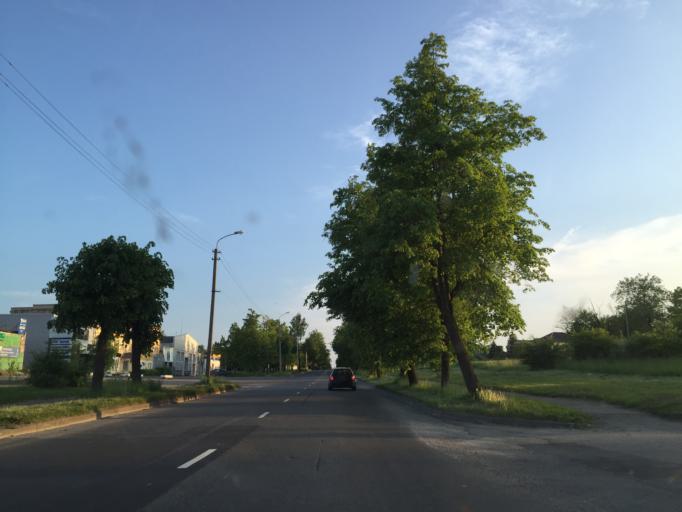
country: LT
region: Siauliu apskritis
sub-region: Siauliai
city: Siauliai
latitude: 55.9477
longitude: 23.3210
